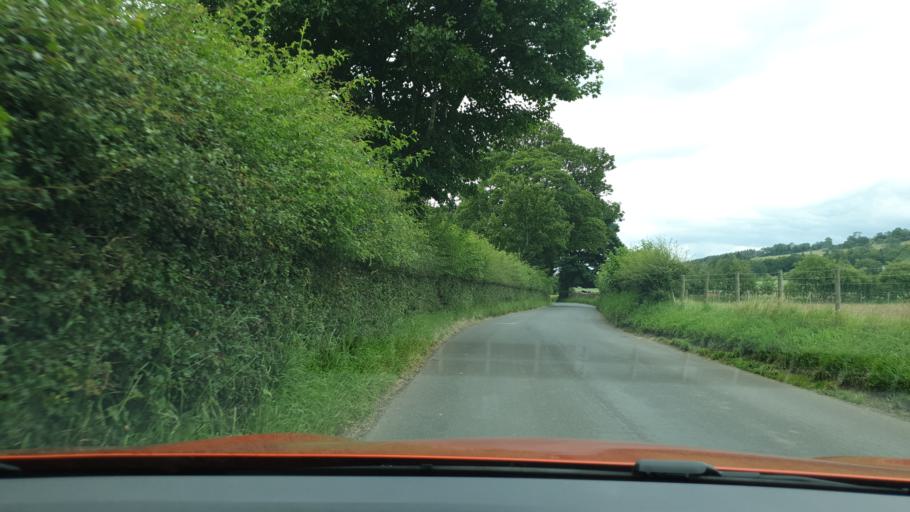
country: GB
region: England
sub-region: Cumbria
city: Penrith
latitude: 54.6064
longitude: -2.8205
